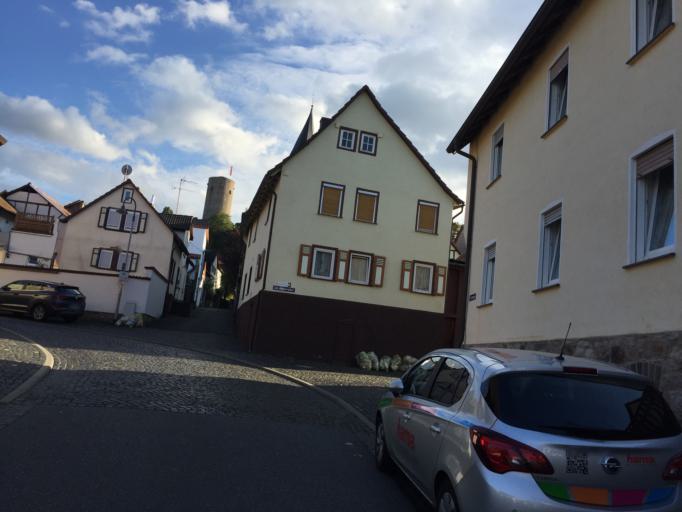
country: DE
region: Hesse
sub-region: Regierungsbezirk Darmstadt
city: Munzenberg
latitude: 50.4535
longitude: 8.7761
